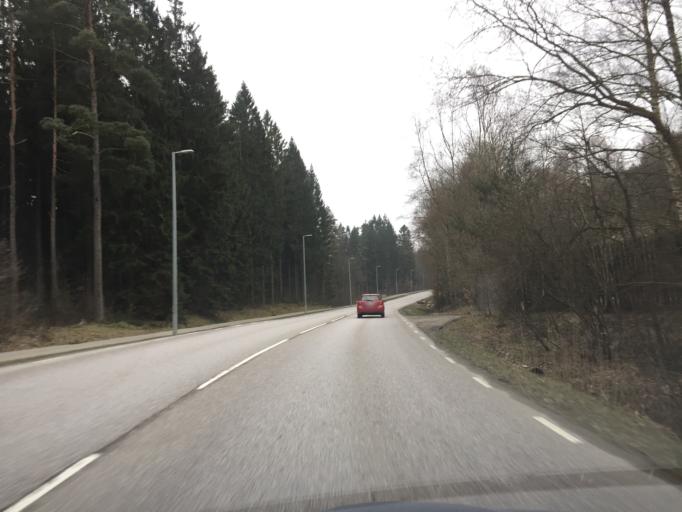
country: SE
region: Vaestra Goetaland
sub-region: Goteborg
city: Eriksbo
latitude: 57.7688
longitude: 12.0755
